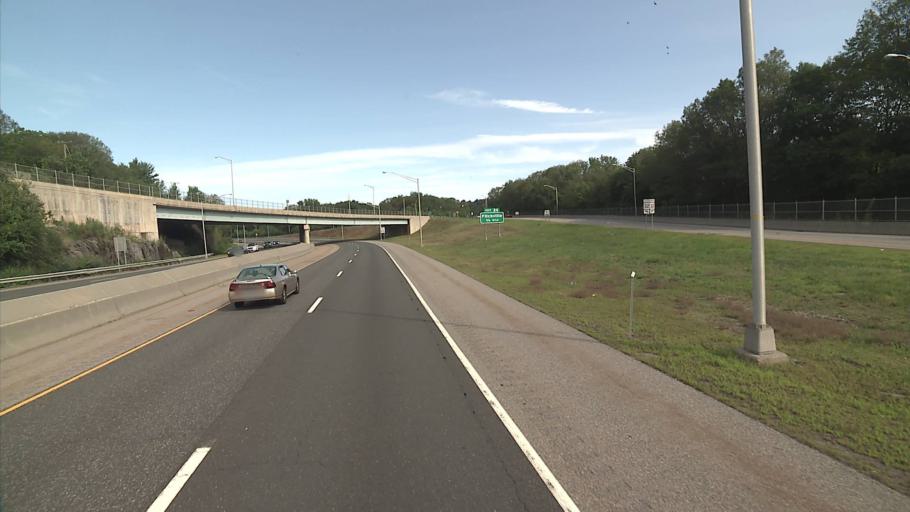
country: US
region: Connecticut
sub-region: New London County
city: Norwich
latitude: 41.5606
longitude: -72.1258
